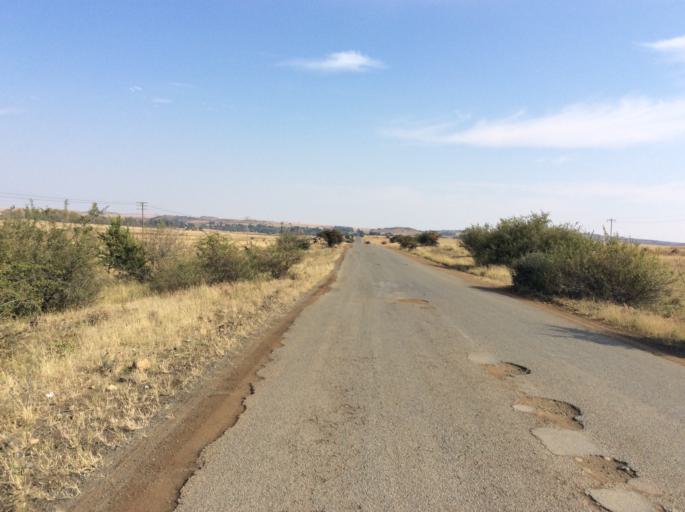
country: LS
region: Mafeteng
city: Mafeteng
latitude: -29.7184
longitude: 27.0043
